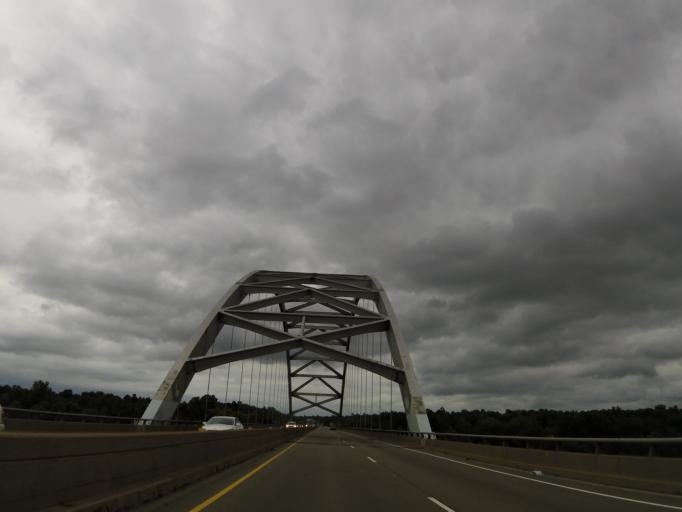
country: US
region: Illinois
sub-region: Massac County
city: Metropolis
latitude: 37.1364
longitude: -88.6861
